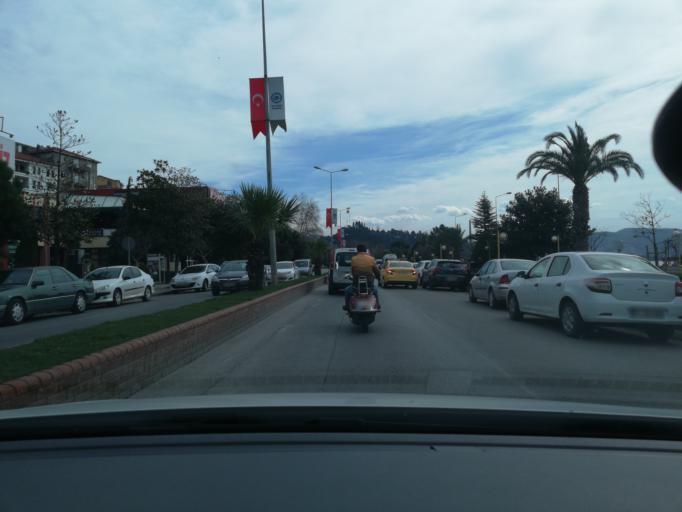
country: TR
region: Zonguldak
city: Eregli
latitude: 41.2829
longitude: 31.4148
